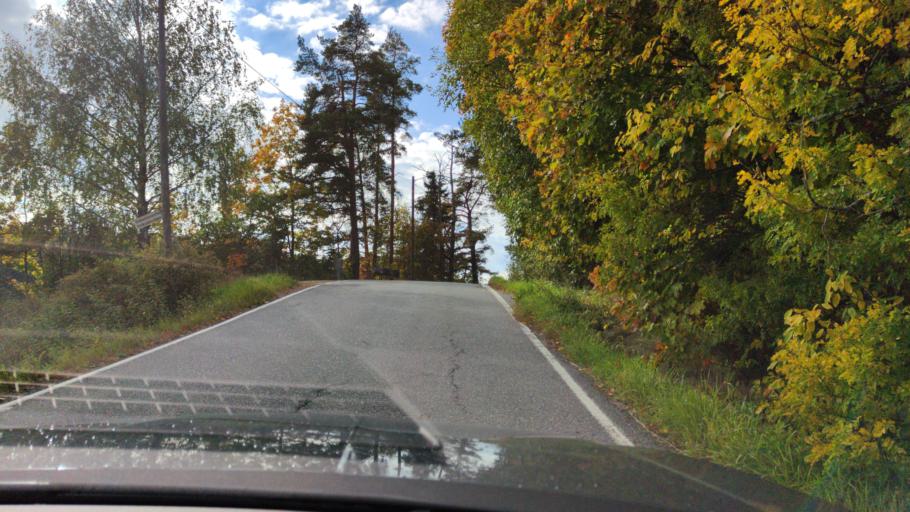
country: FI
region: Varsinais-Suomi
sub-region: Aboland-Turunmaa
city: Pargas
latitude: 60.3488
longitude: 22.2124
